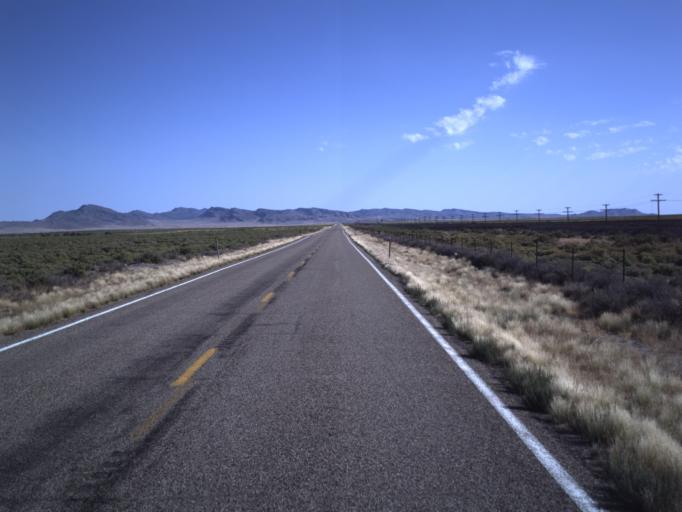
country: US
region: Utah
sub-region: Beaver County
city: Milford
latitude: 38.6304
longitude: -112.9842
